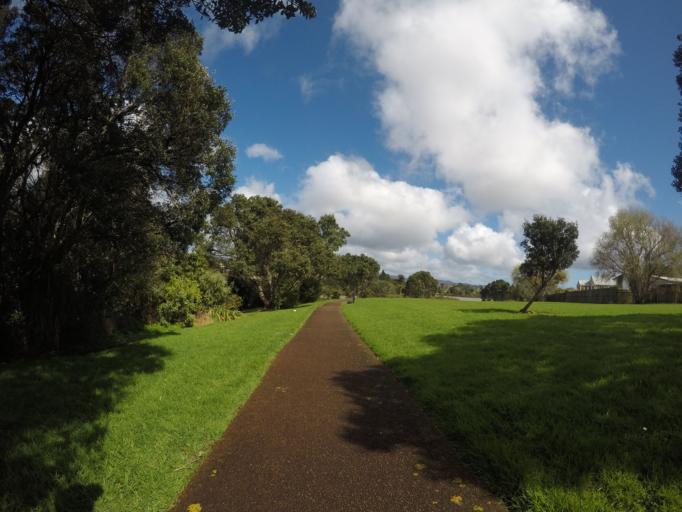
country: NZ
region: Auckland
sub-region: Auckland
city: Rosebank
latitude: -36.8976
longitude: 174.6796
